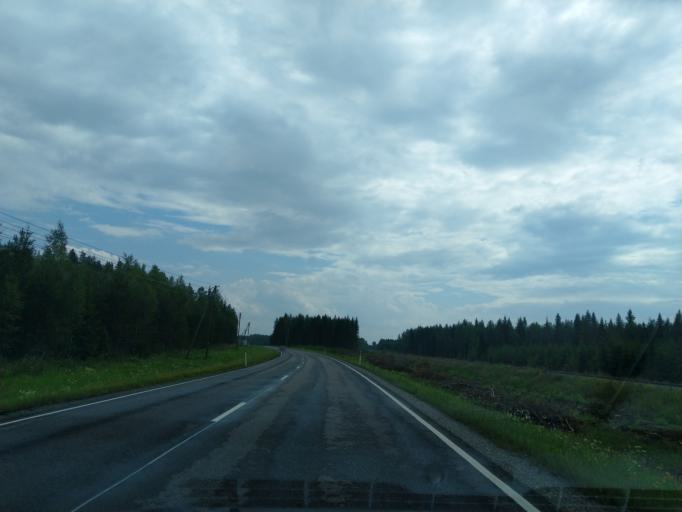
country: FI
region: South Karelia
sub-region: Imatra
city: Parikkala
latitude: 61.6281
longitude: 29.4331
